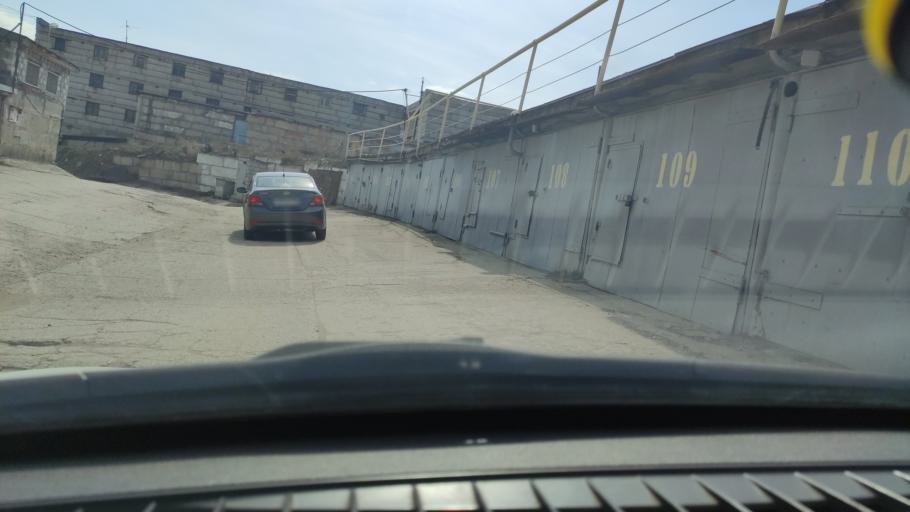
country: RU
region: Samara
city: Zhigulevsk
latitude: 53.4895
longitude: 49.4786
